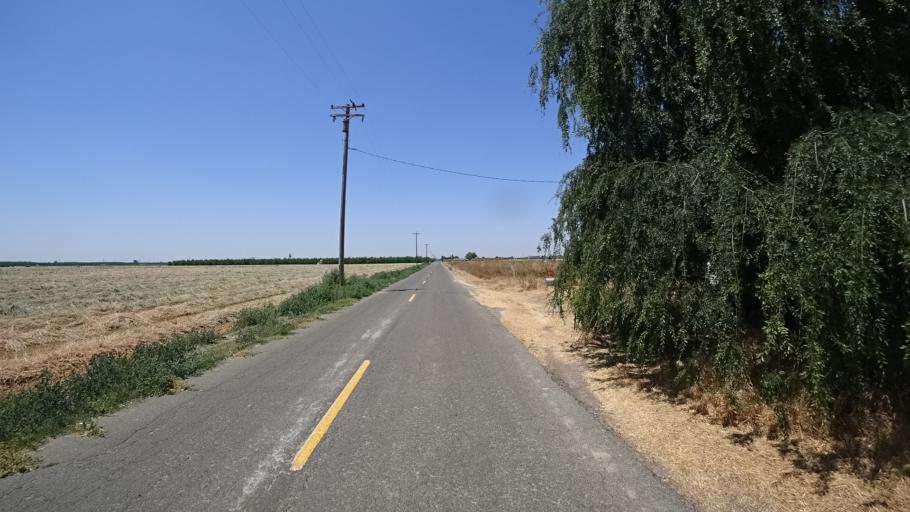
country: US
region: California
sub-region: Fresno County
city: Laton
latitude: 36.3864
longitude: -119.7303
